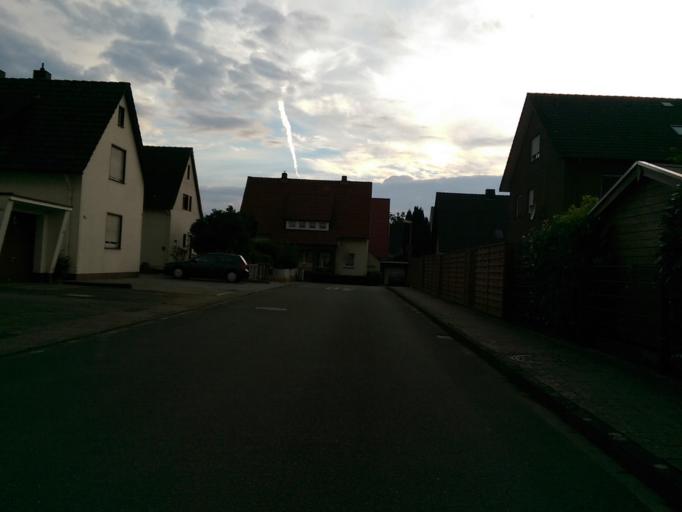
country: DE
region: North Rhine-Westphalia
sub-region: Regierungsbezirk Detmold
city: Guetersloh
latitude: 51.8817
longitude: 8.3882
